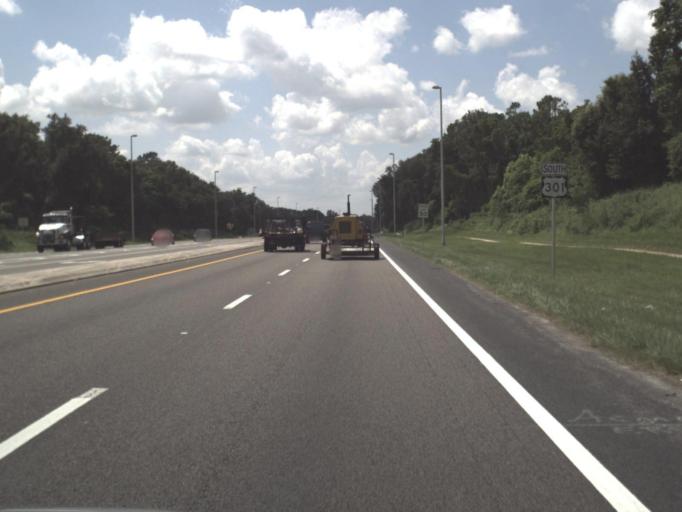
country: US
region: Florida
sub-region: Hillsborough County
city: Temple Terrace
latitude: 28.0324
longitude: -82.3492
